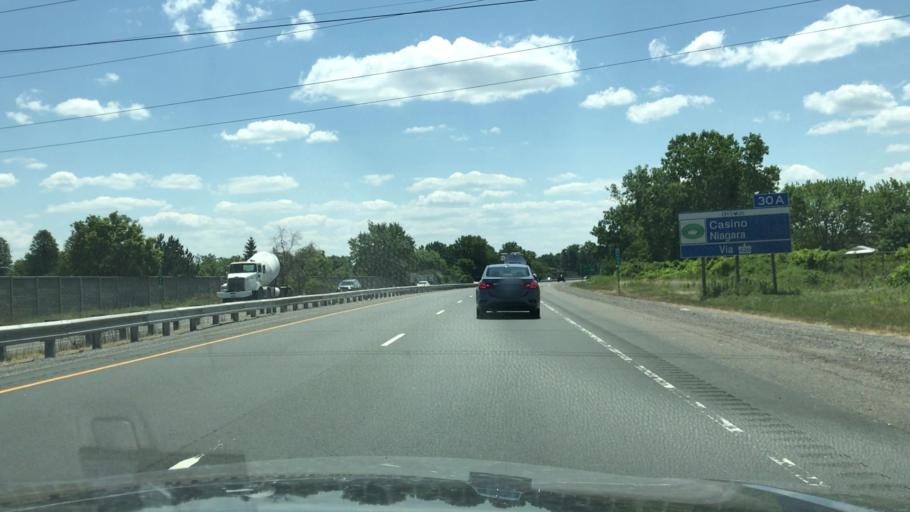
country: CA
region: Ontario
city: Niagara Falls
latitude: 43.1279
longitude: -79.1247
